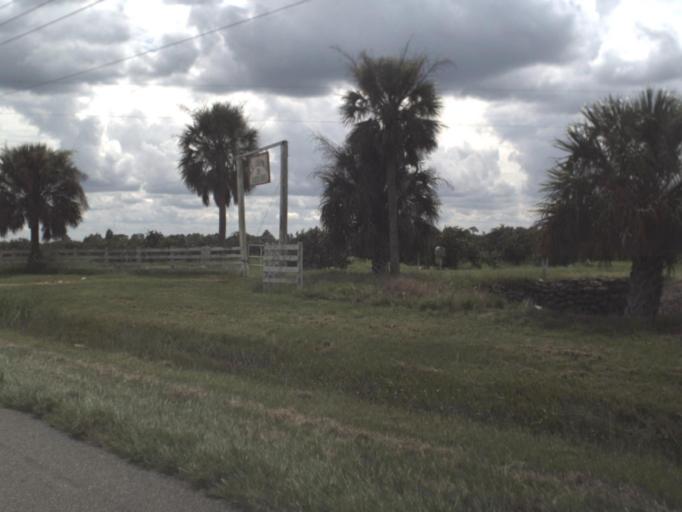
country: US
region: Florida
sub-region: DeSoto County
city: Nocatee
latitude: 27.0272
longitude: -81.7669
